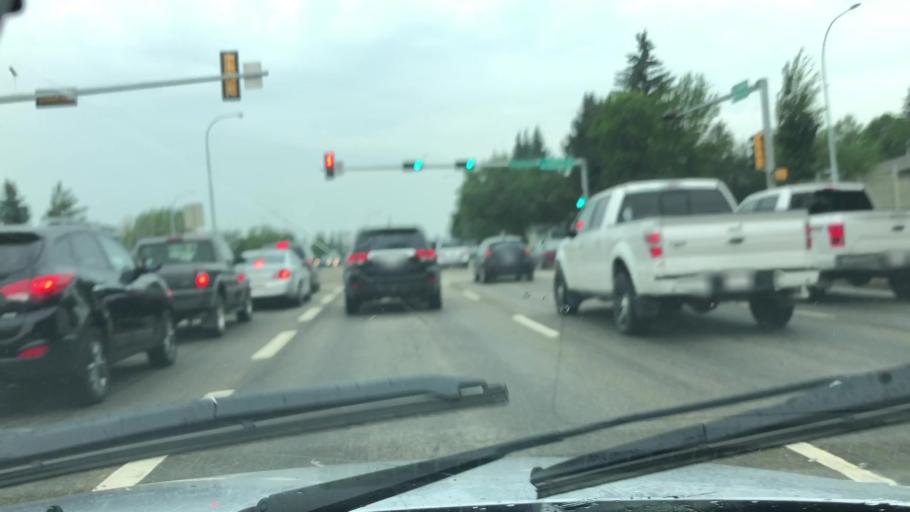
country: CA
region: Alberta
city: St. Albert
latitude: 53.6274
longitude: -113.6183
